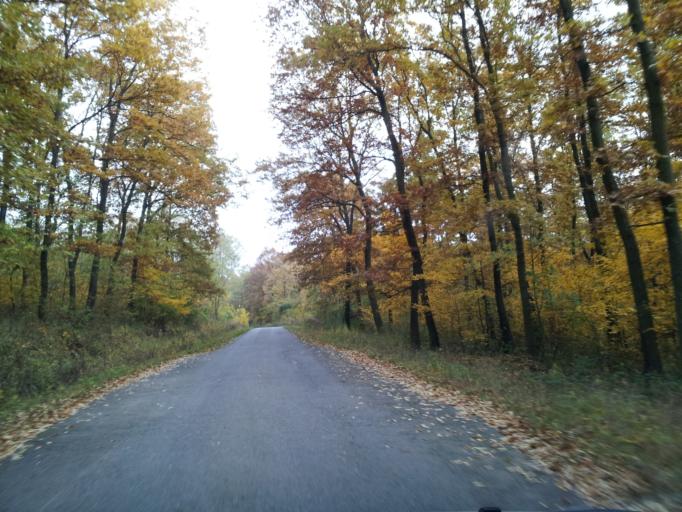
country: HU
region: Gyor-Moson-Sopron
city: Pannonhalma
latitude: 47.4973
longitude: 17.7357
